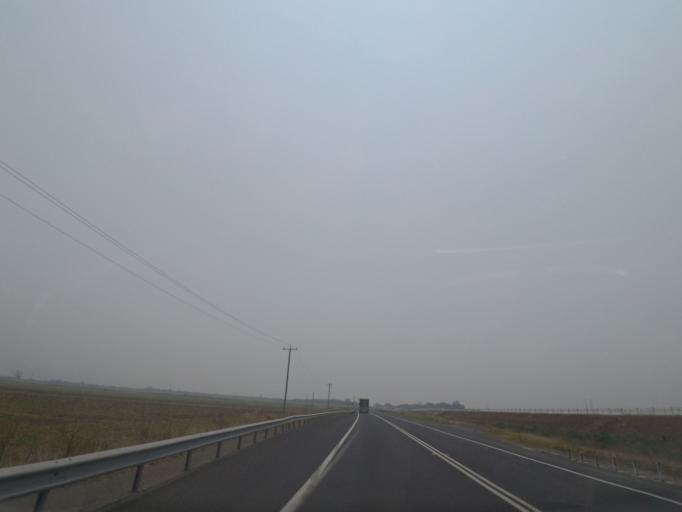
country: AU
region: New South Wales
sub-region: Clarence Valley
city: Maclean
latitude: -29.4115
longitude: 153.2416
